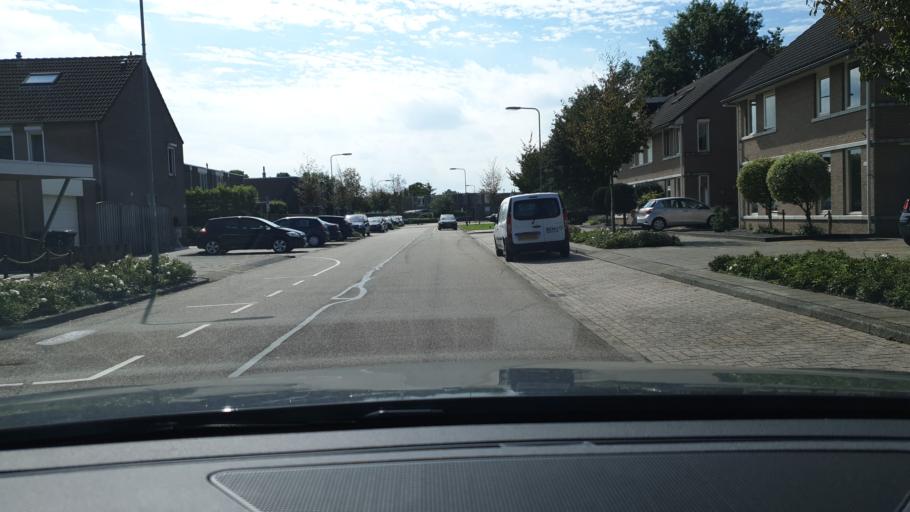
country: NL
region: Limburg
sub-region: Gemeente Venray
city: Venray
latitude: 51.5353
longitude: 5.9957
